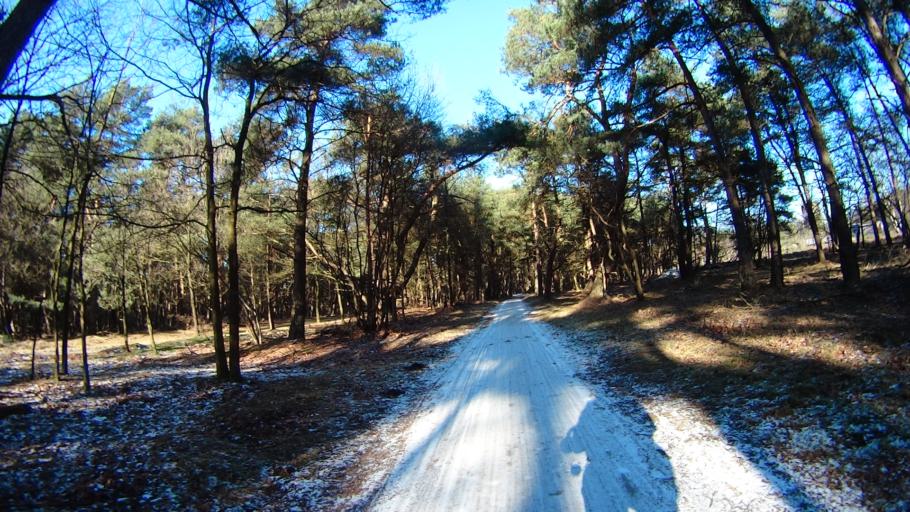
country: NL
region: North Holland
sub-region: Gemeente Laren
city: Laren
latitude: 52.2566
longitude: 5.2024
